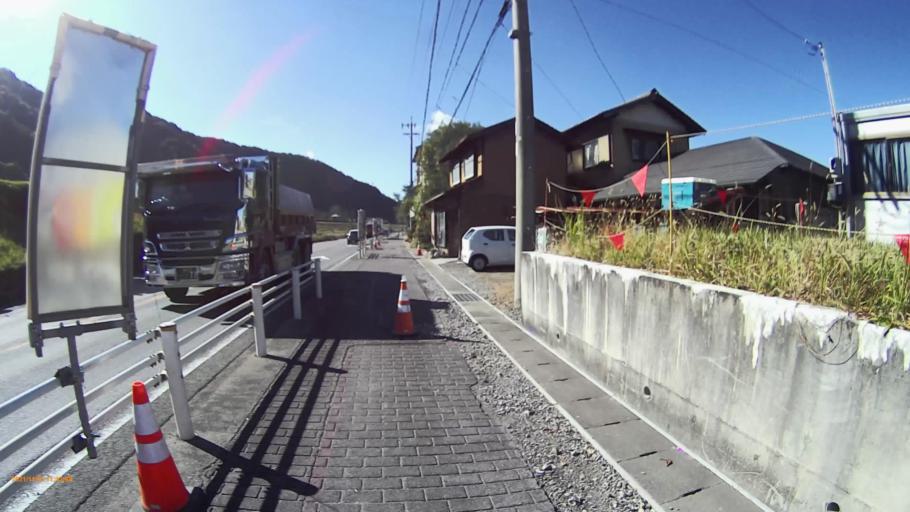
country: JP
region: Gifu
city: Inuyama
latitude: 35.4249
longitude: 136.9817
